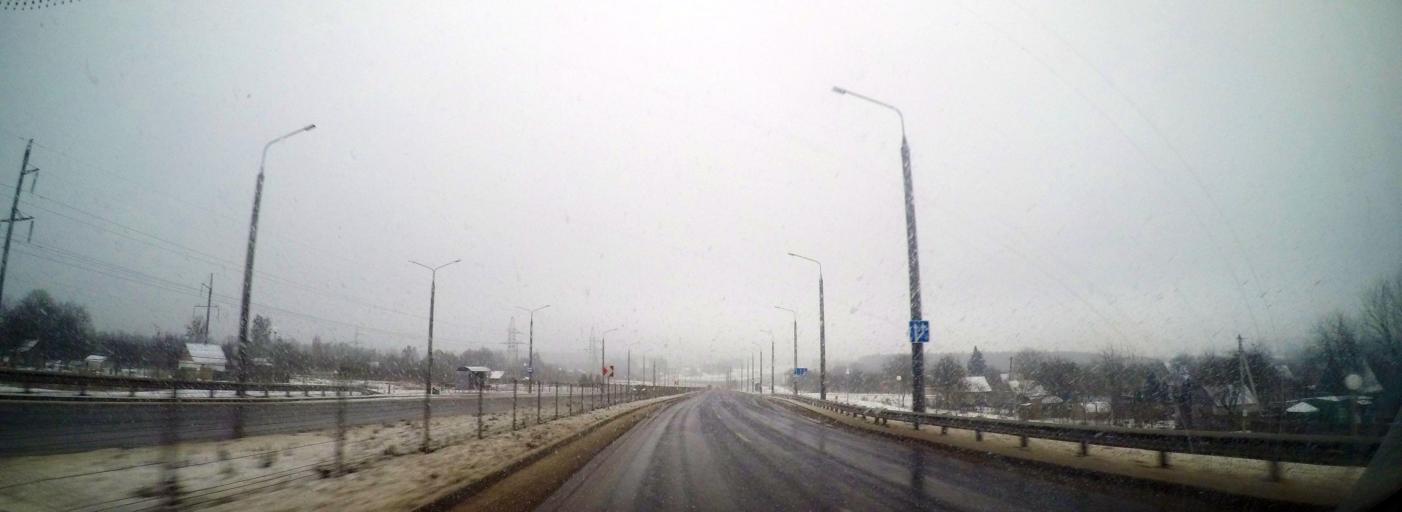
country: BY
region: Grodnenskaya
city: Hrodna
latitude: 53.6598
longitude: 23.8874
